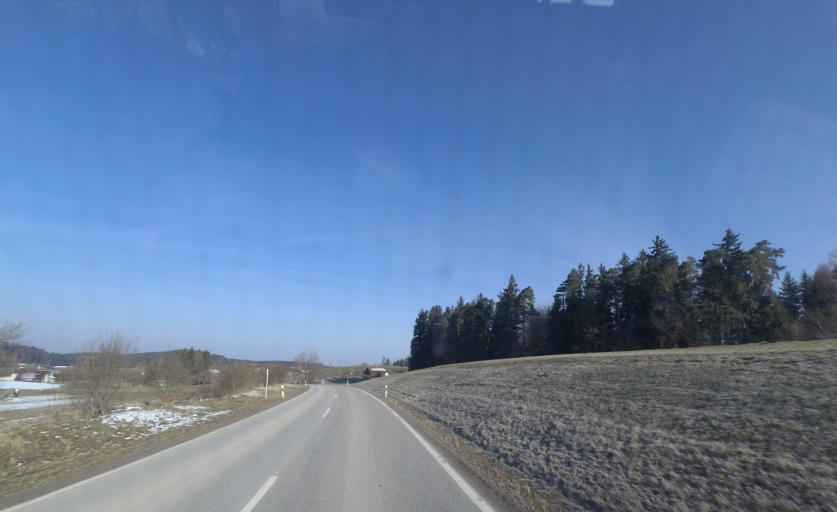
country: DE
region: Bavaria
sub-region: Upper Bavaria
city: Traunreut
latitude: 47.9408
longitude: 12.5525
